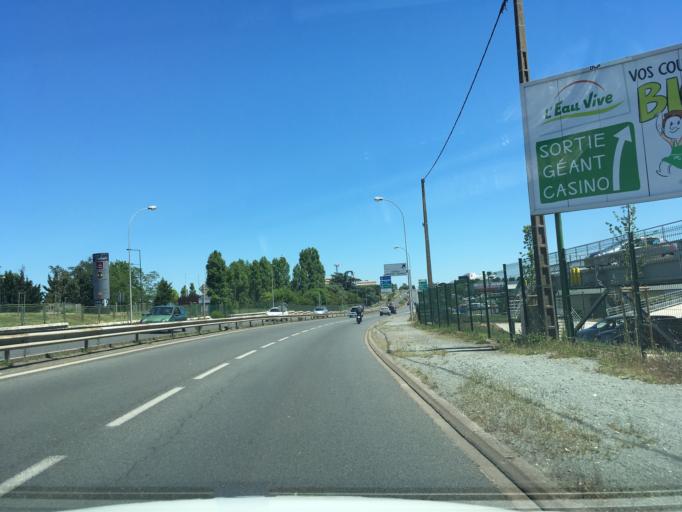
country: FR
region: Poitou-Charentes
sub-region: Departement des Deux-Sevres
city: Chauray
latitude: 46.3384
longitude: -0.4155
